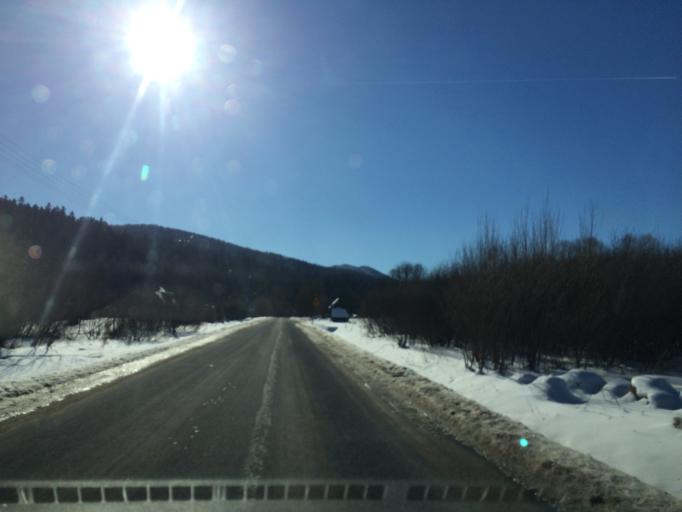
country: PL
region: Subcarpathian Voivodeship
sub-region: Powiat bieszczadzki
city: Lutowiska
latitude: 49.1662
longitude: 22.6911
